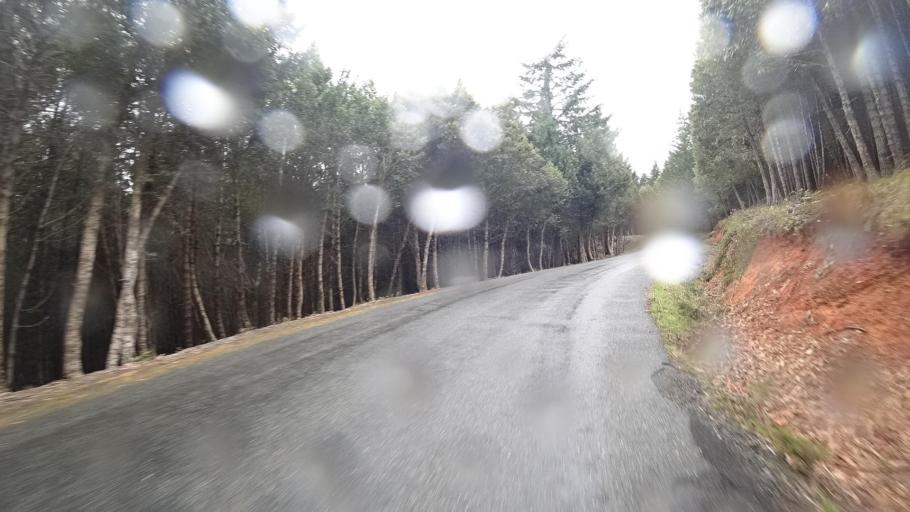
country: US
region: California
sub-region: Humboldt County
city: Willow Creek
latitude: 41.2001
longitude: -123.7925
